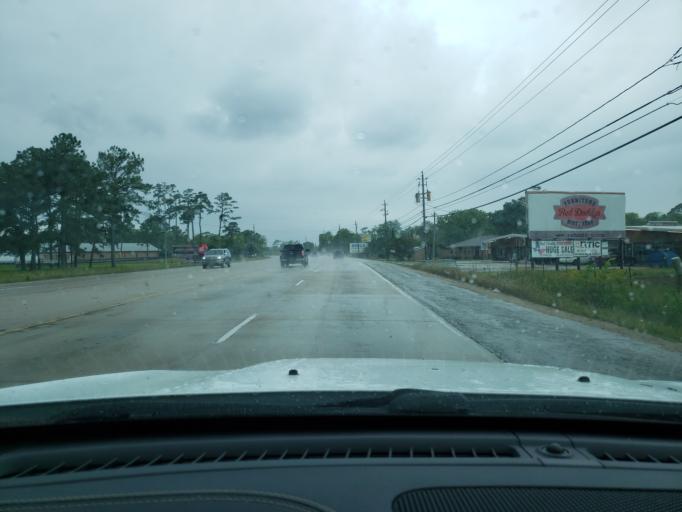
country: US
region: Texas
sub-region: Chambers County
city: Mont Belvieu
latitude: 29.7944
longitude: -94.9085
